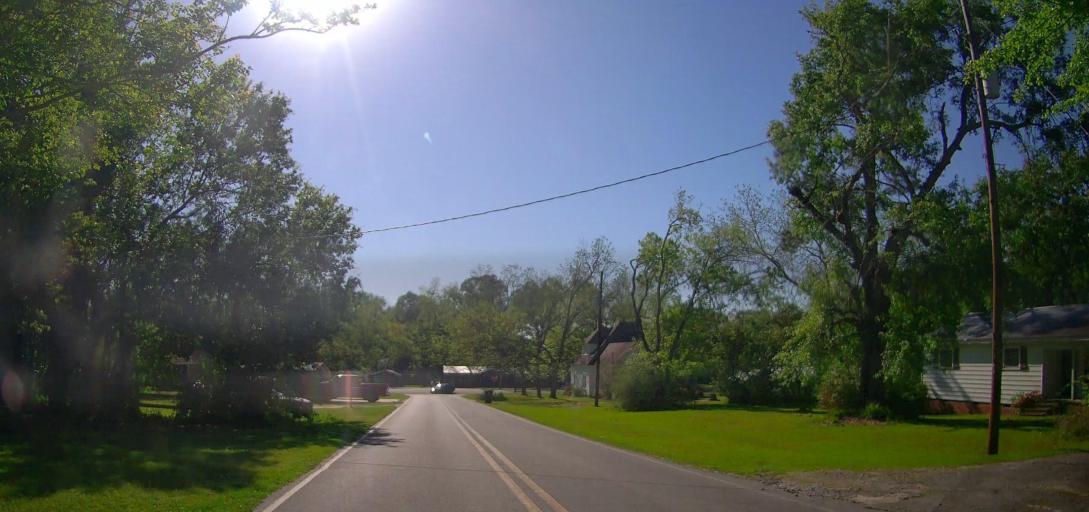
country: US
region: Georgia
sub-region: Wilcox County
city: Rochelle
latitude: 31.9464
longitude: -83.4552
